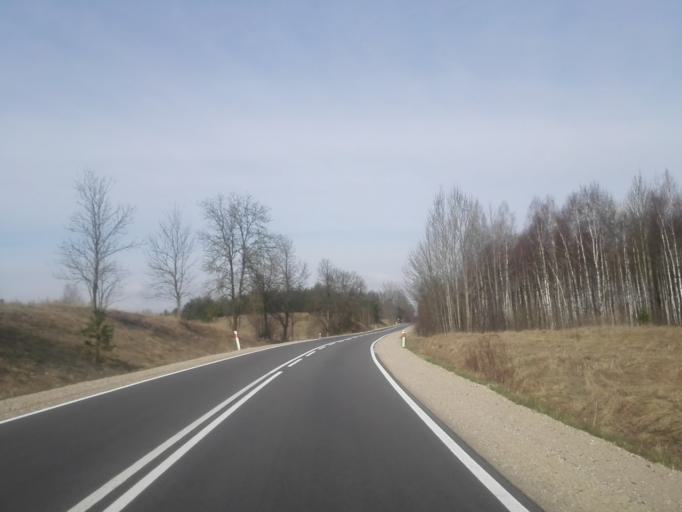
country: PL
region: Podlasie
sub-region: Powiat sejnenski
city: Sejny
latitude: 54.0680
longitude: 23.3560
